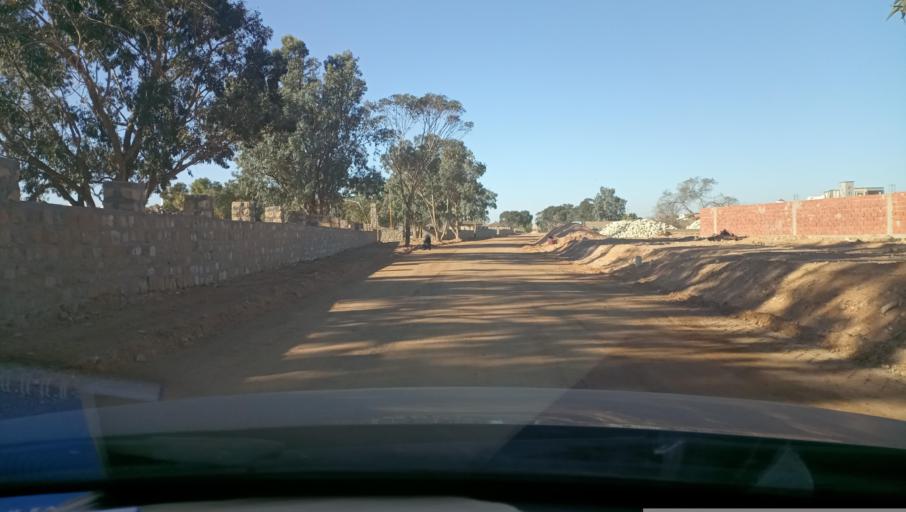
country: TN
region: Madanin
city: Medenine
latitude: 33.1812
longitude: 10.4417
